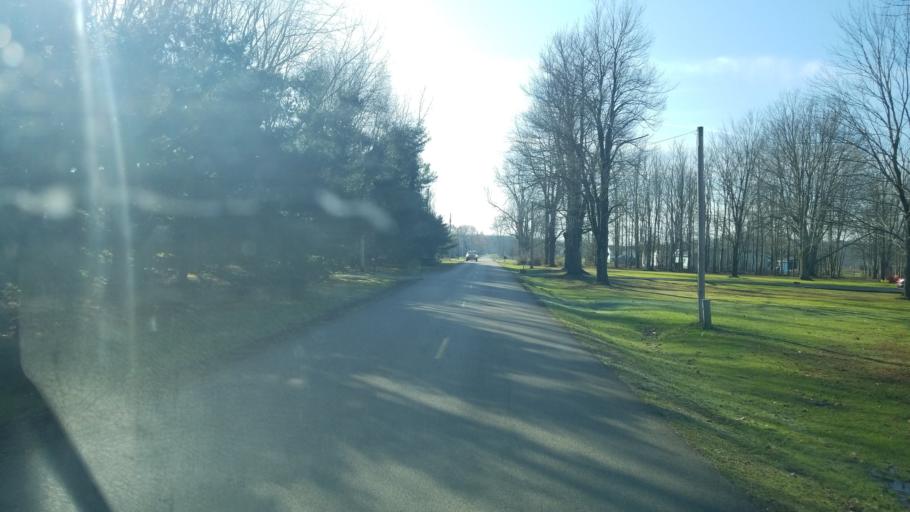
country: US
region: Ohio
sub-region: Ashtabula County
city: Jefferson
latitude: 41.7585
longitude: -80.7258
